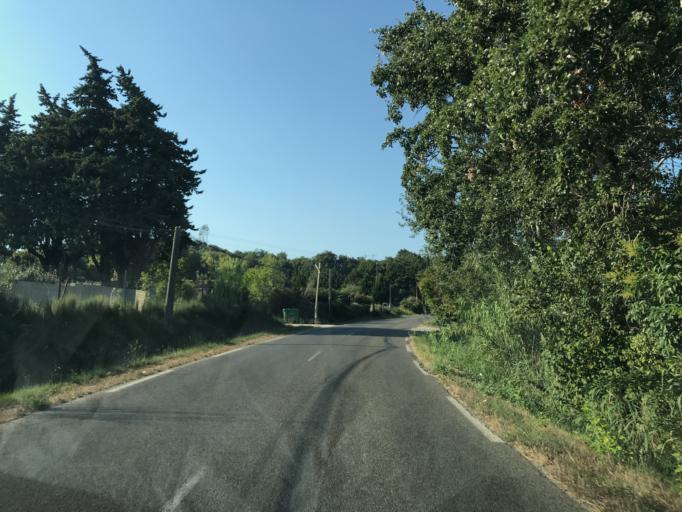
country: FR
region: Provence-Alpes-Cote d'Azur
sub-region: Departement des Bouches-du-Rhone
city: Saint-Chamas
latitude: 43.5641
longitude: 5.0157
